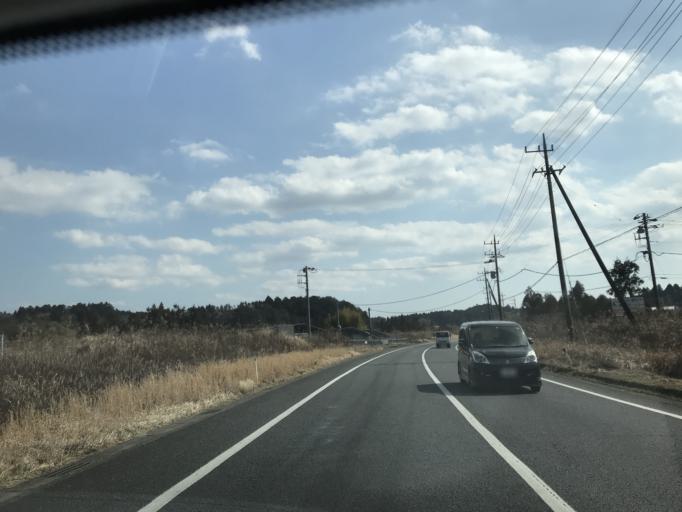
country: JP
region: Chiba
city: Sawara
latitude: 35.8216
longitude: 140.5171
